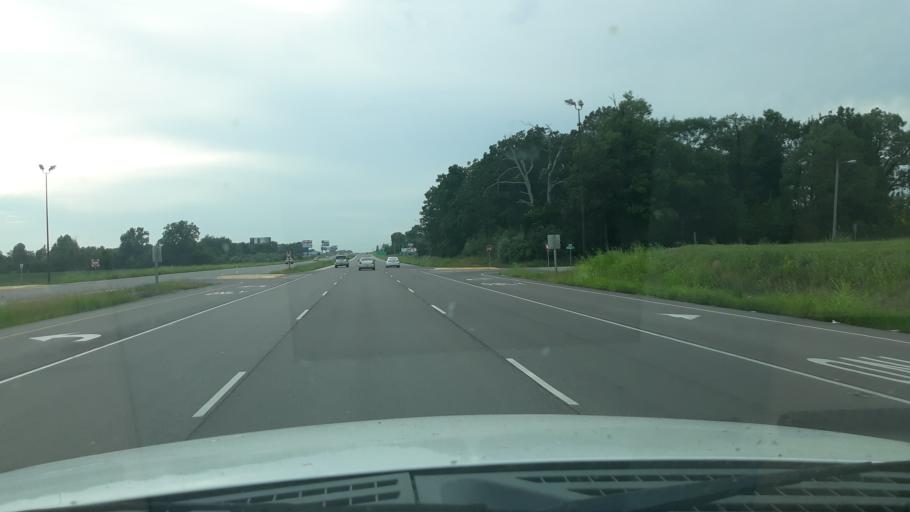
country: US
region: Illinois
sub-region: Williamson County
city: Energy
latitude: 37.7451
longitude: -89.0346
